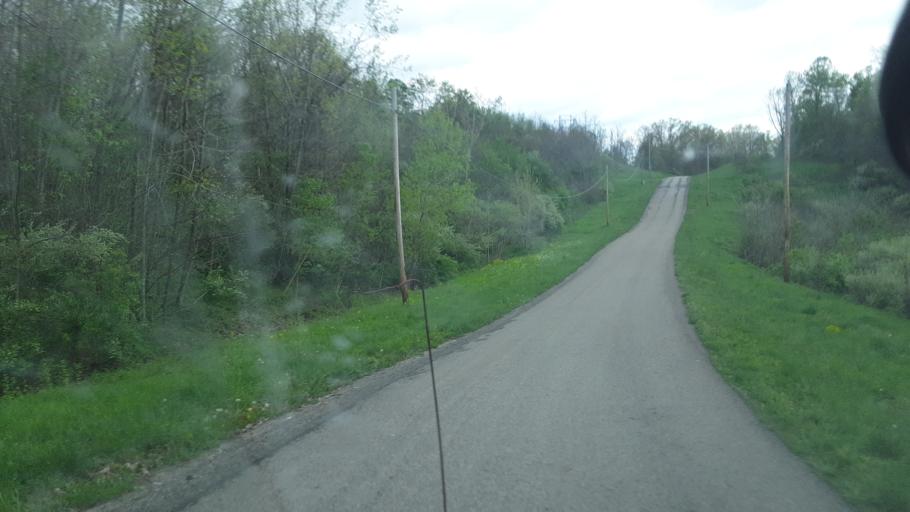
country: US
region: Ohio
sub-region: Noble County
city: Caldwell
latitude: 39.7314
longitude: -81.6812
